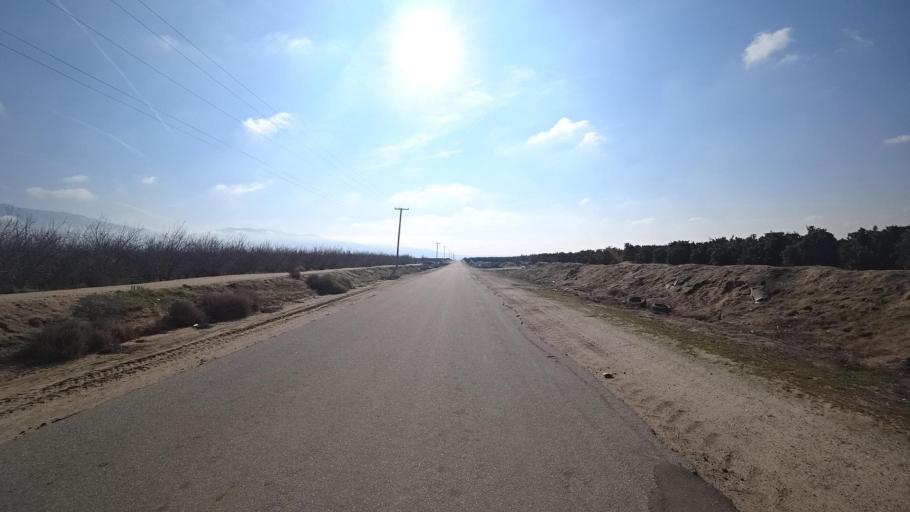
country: US
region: California
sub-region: Kern County
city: Arvin
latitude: 35.2736
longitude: -118.7889
